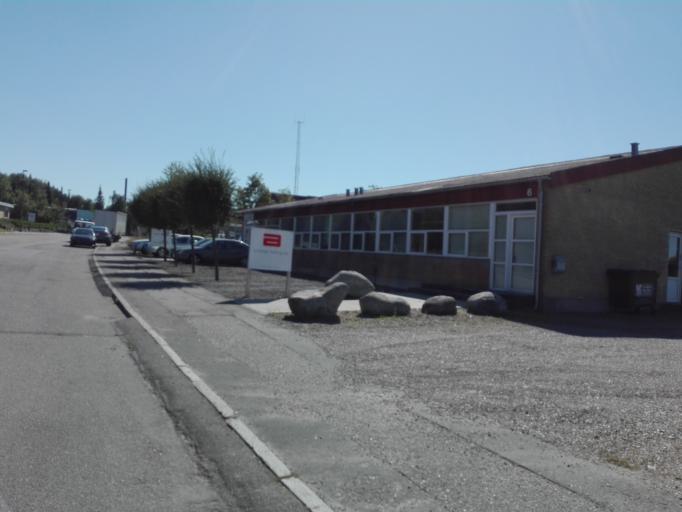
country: DK
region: Central Jutland
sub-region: Arhus Kommune
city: Stavtrup
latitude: 56.1141
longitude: 10.1415
